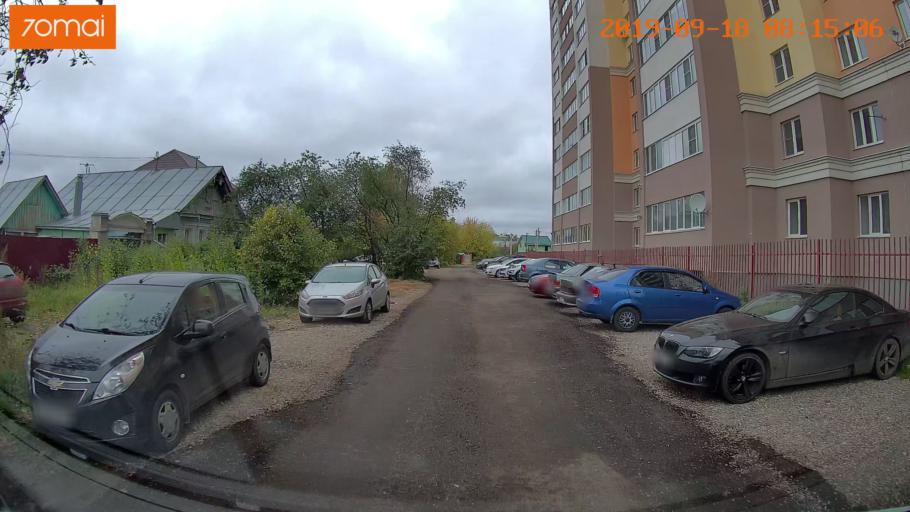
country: RU
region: Ivanovo
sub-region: Gorod Ivanovo
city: Ivanovo
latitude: 56.9748
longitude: 41.0024
